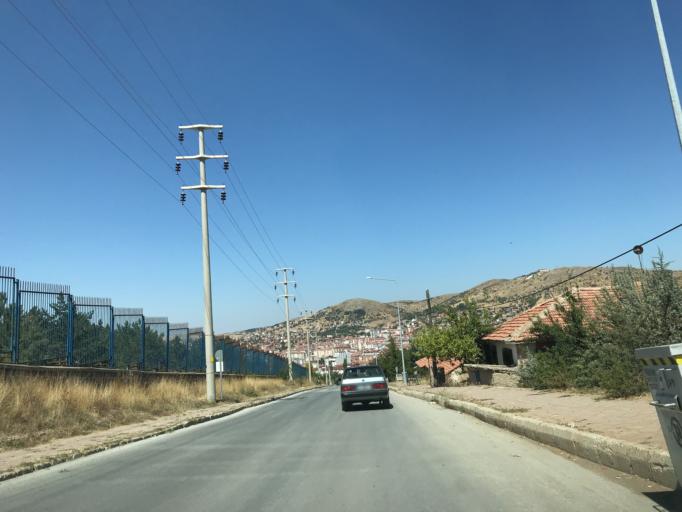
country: TR
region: Yozgat
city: Yozgat
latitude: 39.8159
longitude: 34.8219
